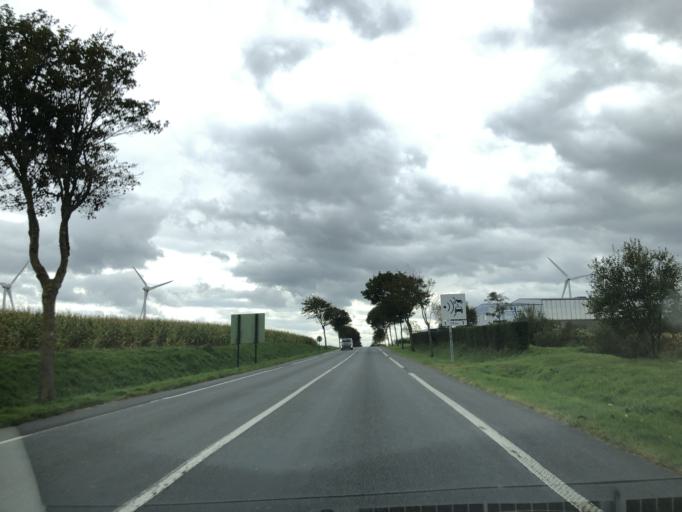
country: FR
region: Nord-Pas-de-Calais
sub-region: Departement du Pas-de-Calais
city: Fruges
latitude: 50.4986
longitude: 2.1293
